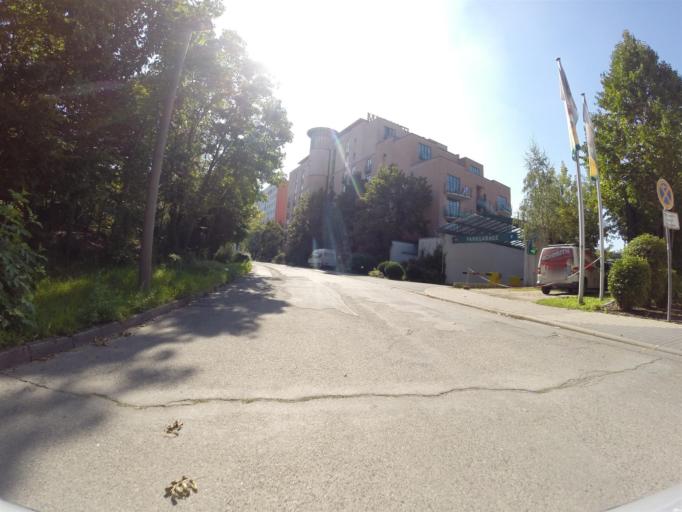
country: DE
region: Thuringia
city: Sulza
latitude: 50.8810
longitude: 11.6002
